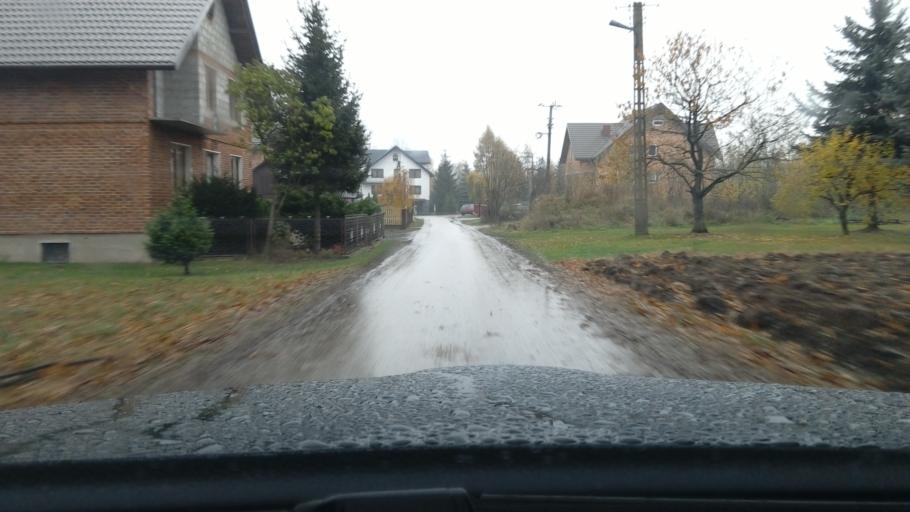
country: PL
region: Lodz Voivodeship
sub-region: Powiat skierniewicki
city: Godzianow
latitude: 51.9017
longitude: 20.0498
